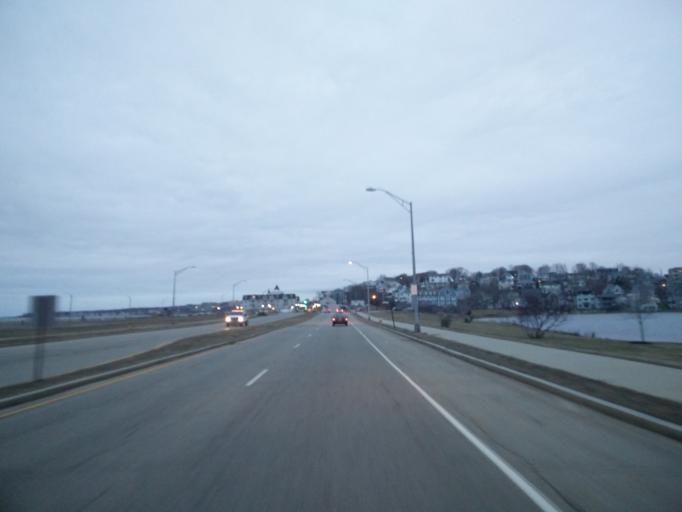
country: US
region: Massachusetts
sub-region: Plymouth County
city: Hingham
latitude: 42.2775
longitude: -70.8656
